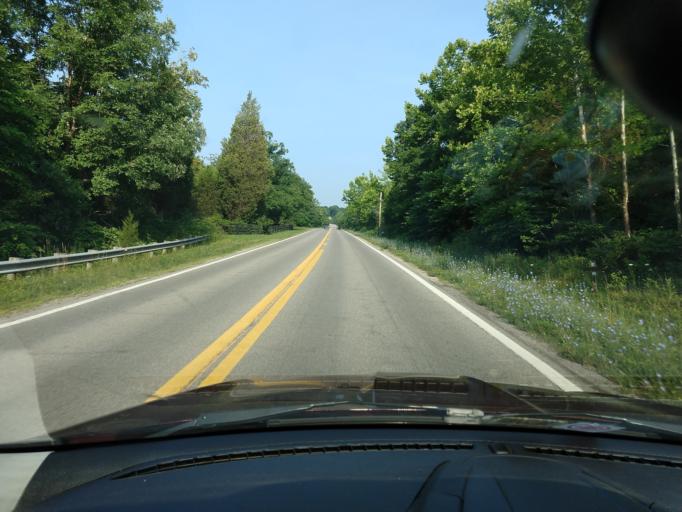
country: US
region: West Virginia
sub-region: Jackson County
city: Ripley
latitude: 38.8397
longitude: -81.7846
